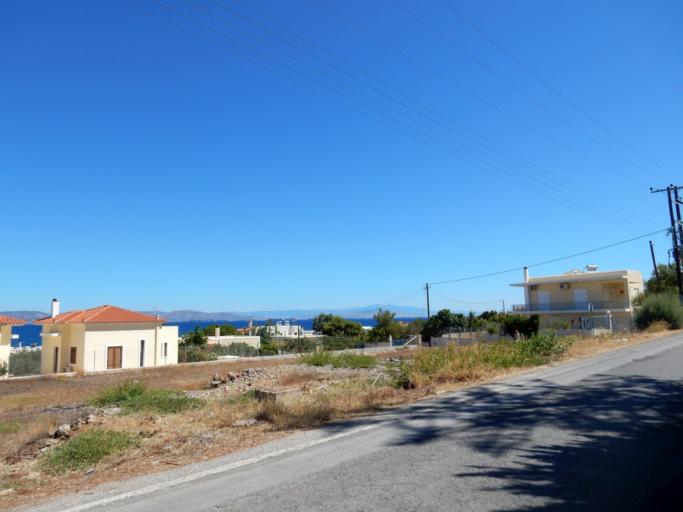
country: GR
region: Attica
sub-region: Nomos Piraios
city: Vathi
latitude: 37.7710
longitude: 23.5018
